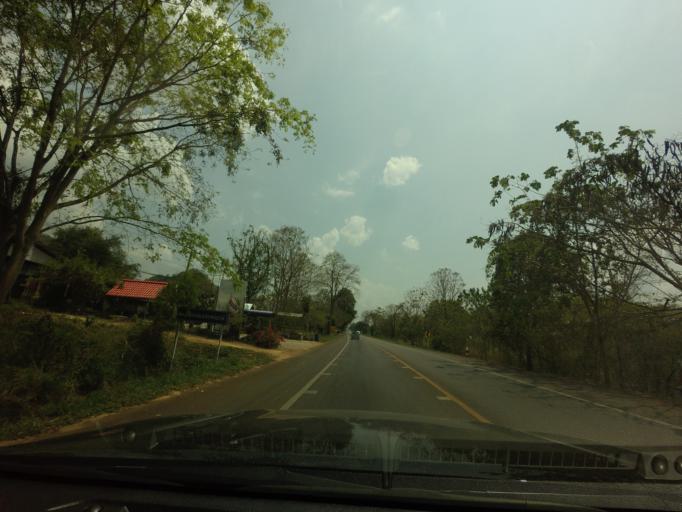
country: TH
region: Kanchanaburi
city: Sai Yok
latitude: 14.1364
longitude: 99.1519
